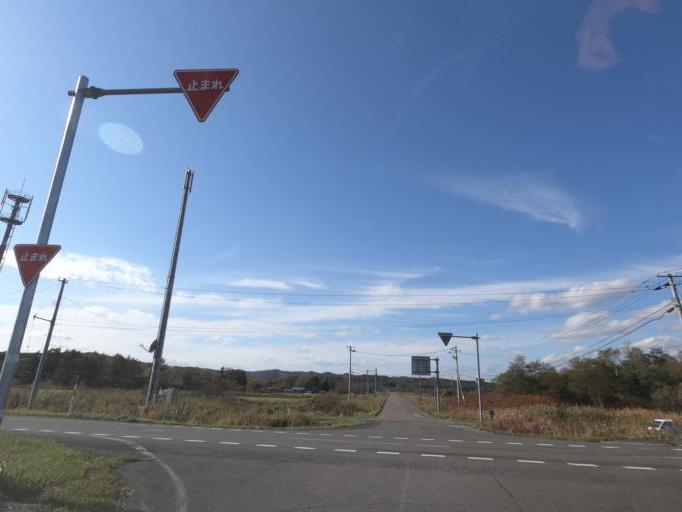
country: JP
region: Hokkaido
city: Obihiro
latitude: 42.6414
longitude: 143.5064
